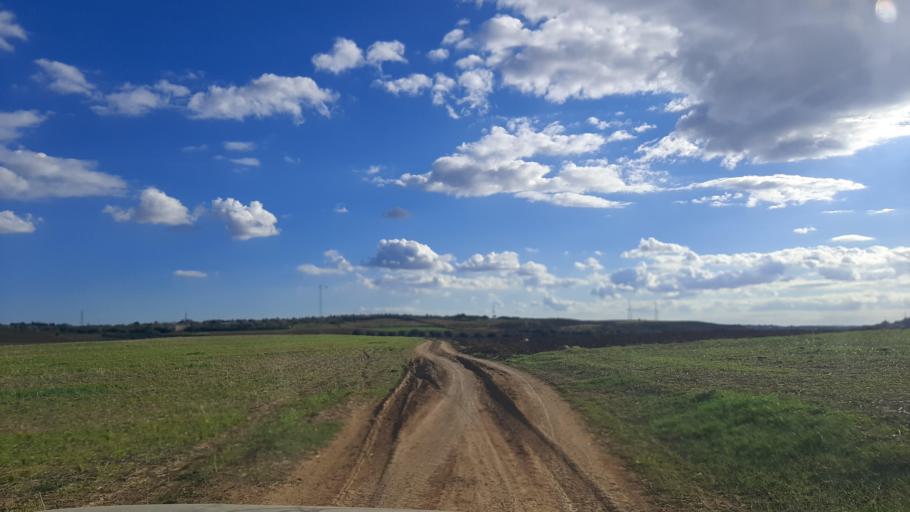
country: TN
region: Nabul
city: Bu `Urqub
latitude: 36.4486
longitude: 10.5013
